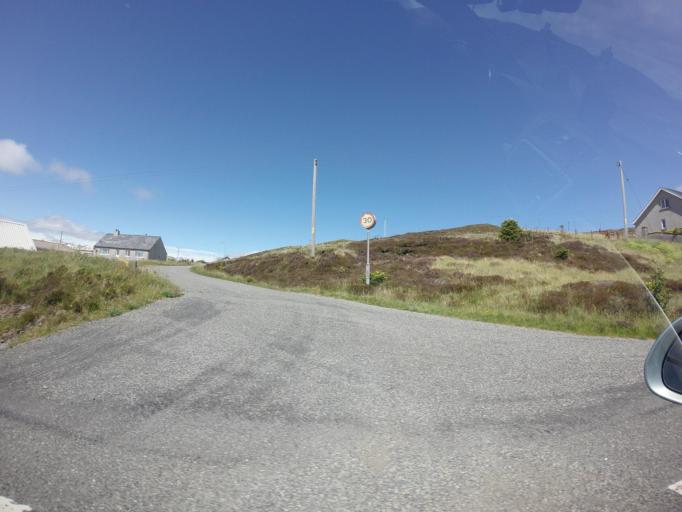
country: GB
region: Scotland
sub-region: Eilean Siar
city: Stornoway
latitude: 58.0916
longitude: -6.6044
